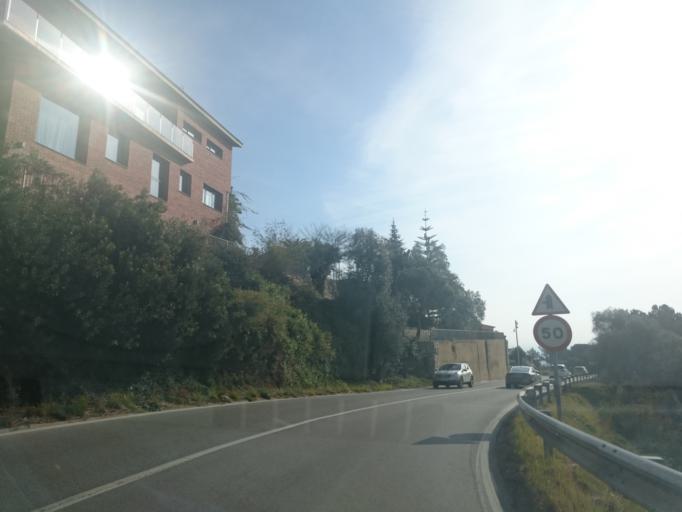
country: ES
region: Catalonia
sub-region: Provincia de Barcelona
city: Begues
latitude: 41.3146
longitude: 1.9652
